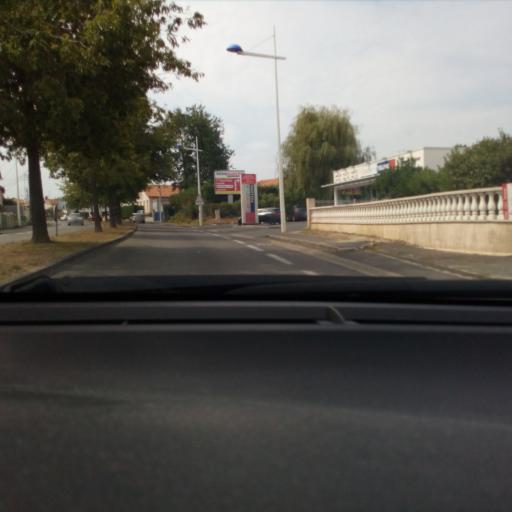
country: FR
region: Poitou-Charentes
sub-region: Departement de la Charente
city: Angouleme
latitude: 45.6645
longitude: 0.1497
